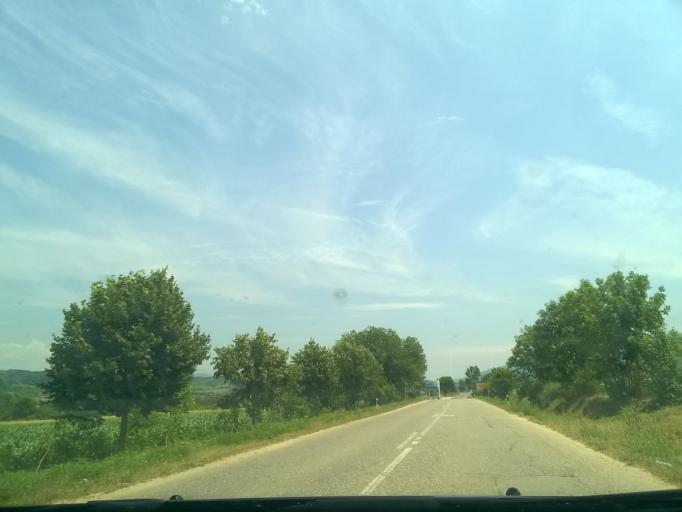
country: RS
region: Central Serbia
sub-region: Zajecarski Okrug
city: Soko Banja
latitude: 43.6534
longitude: 21.8404
